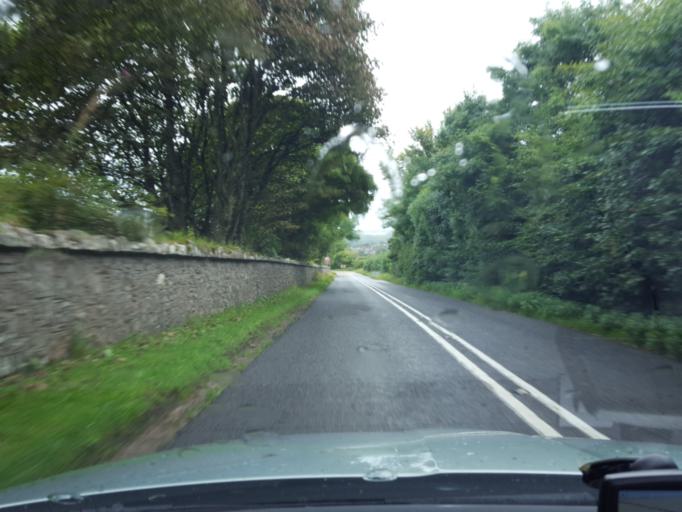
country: GB
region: Scotland
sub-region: Aberdeenshire
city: Stonehaven
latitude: 56.9783
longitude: -2.2432
